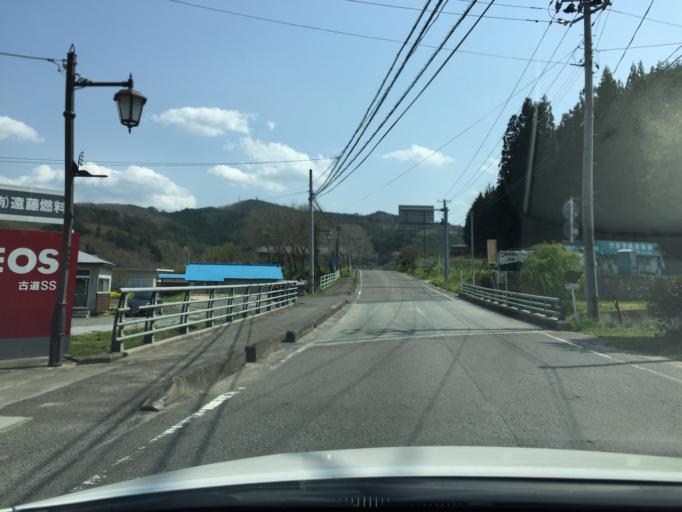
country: JP
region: Fukushima
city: Namie
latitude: 37.4344
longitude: 140.7952
